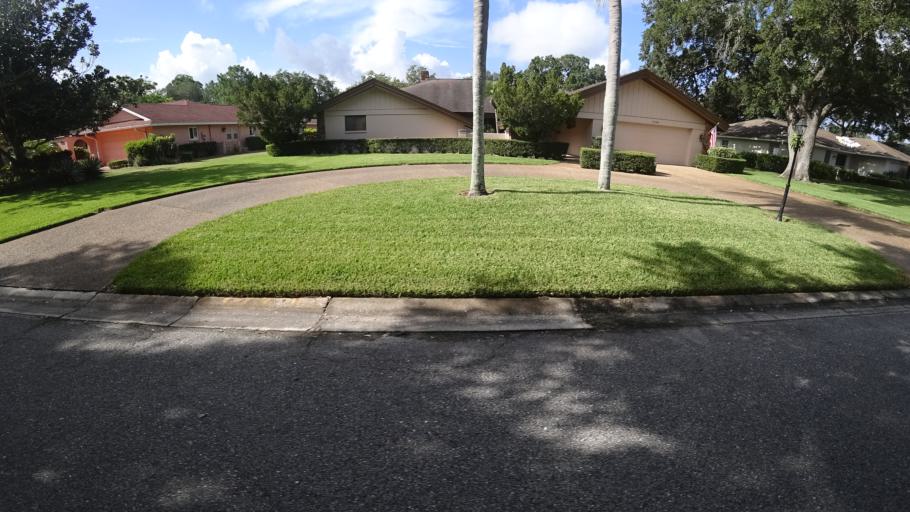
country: US
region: Florida
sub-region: Sarasota County
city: Desoto Lakes
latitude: 27.4025
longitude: -82.4973
